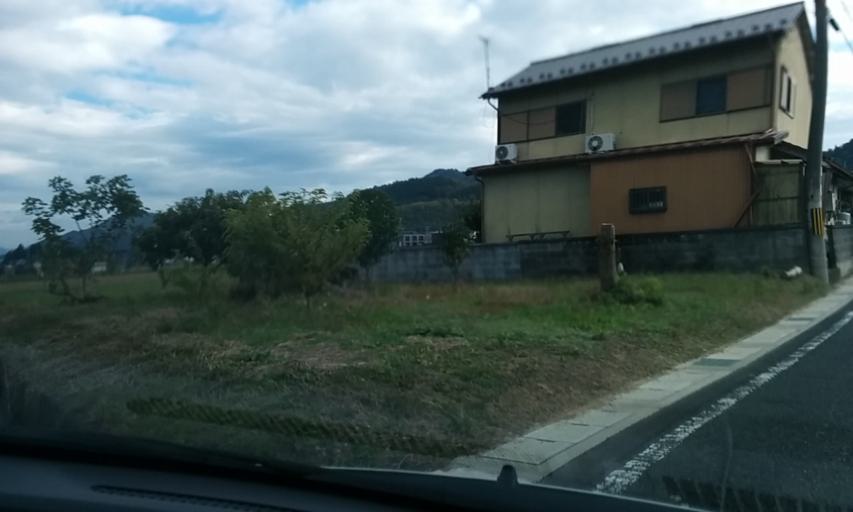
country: JP
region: Kyoto
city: Fukuchiyama
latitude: 35.3042
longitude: 135.1770
